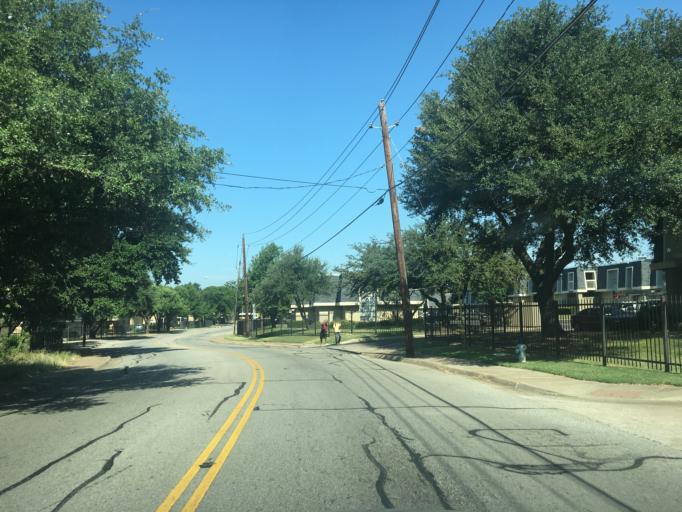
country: US
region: Texas
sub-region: Dallas County
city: Garland
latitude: 32.8529
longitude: -96.6479
